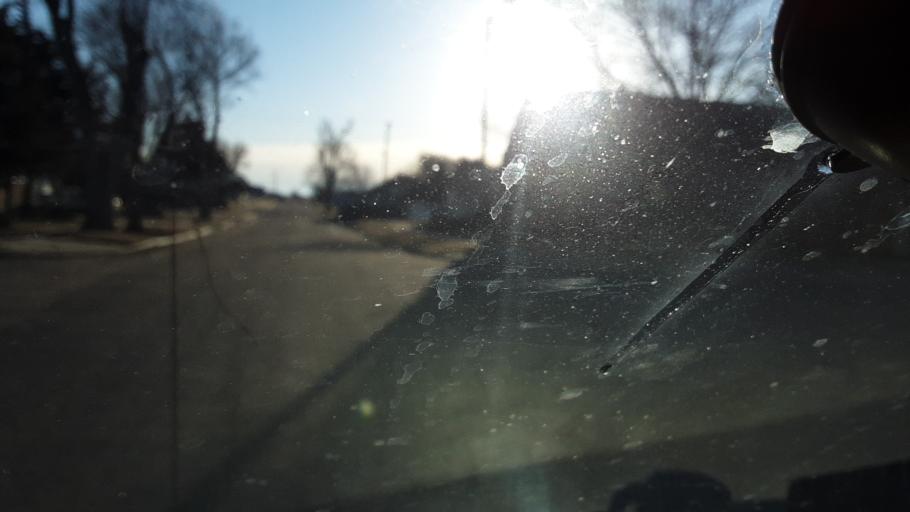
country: US
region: Kansas
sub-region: Rice County
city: Lyons
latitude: 38.3542
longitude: -98.3481
